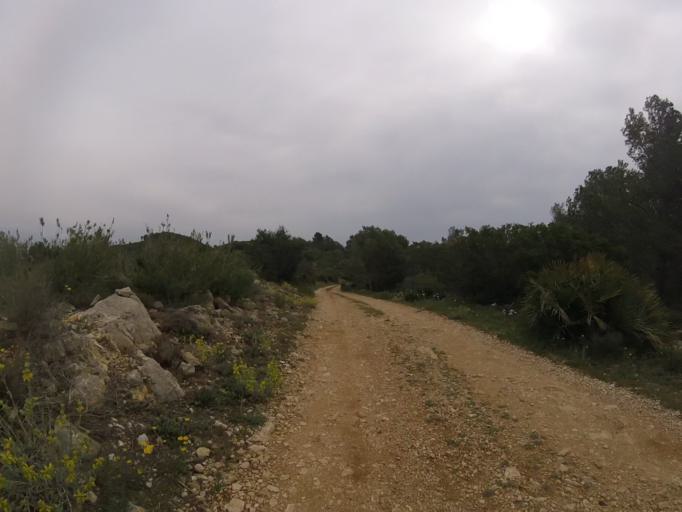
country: ES
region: Valencia
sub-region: Provincia de Castello
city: Alcala de Xivert
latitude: 40.3081
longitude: 0.2581
